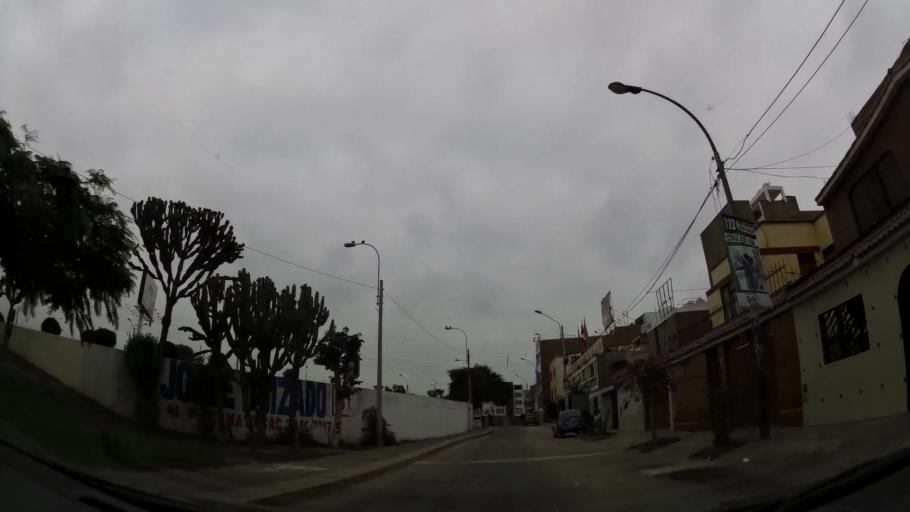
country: PE
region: Callao
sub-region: Callao
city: Callao
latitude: -12.0541
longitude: -77.0989
